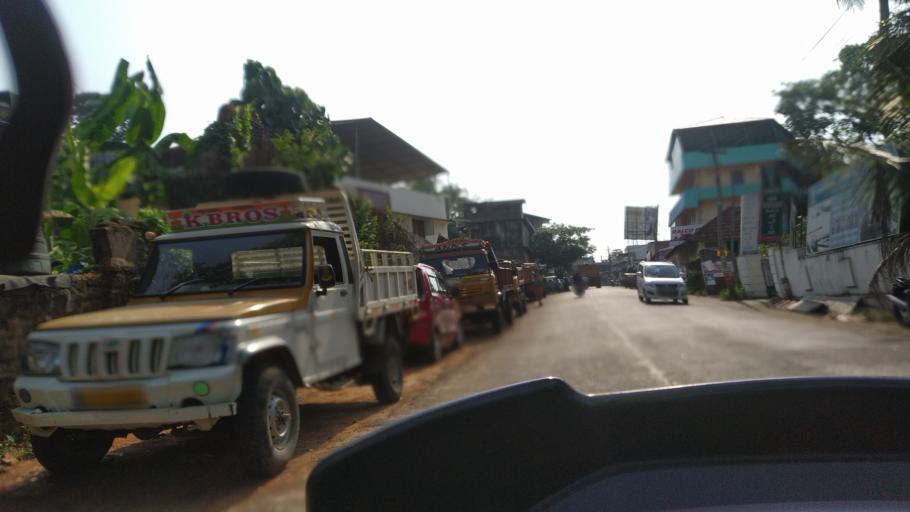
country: IN
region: Kerala
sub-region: Ernakulam
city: Piravam
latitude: 9.8718
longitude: 76.4901
